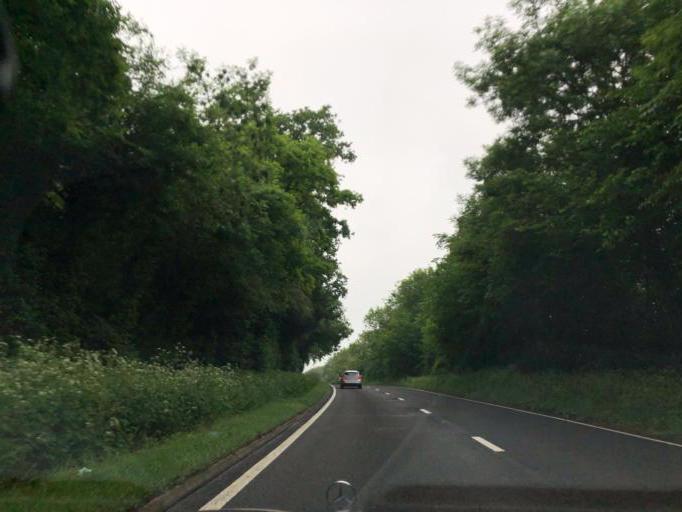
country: GB
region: England
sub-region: Warwickshire
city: Harbury
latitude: 52.2228
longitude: -1.5195
